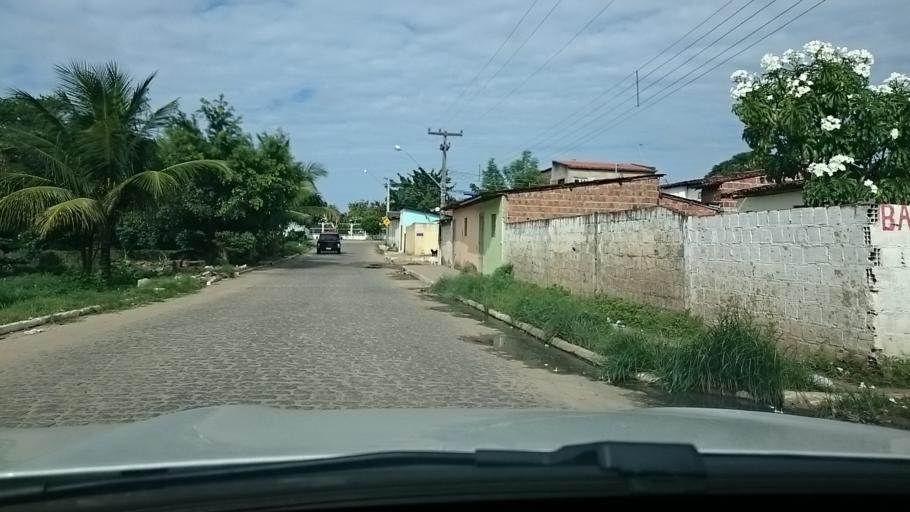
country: BR
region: Paraiba
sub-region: Joao Pessoa
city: Joao Pessoa
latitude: -7.1705
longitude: -34.8545
